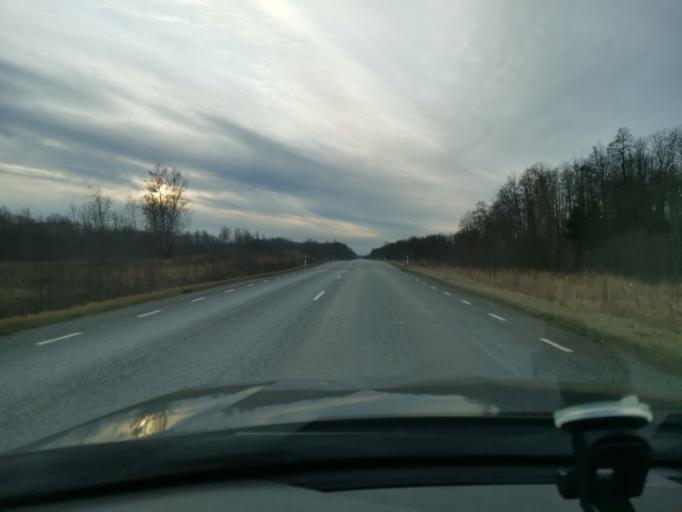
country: EE
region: Ida-Virumaa
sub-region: Narva-Joesuu linn
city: Narva-Joesuu
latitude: 59.3356
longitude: 27.9654
